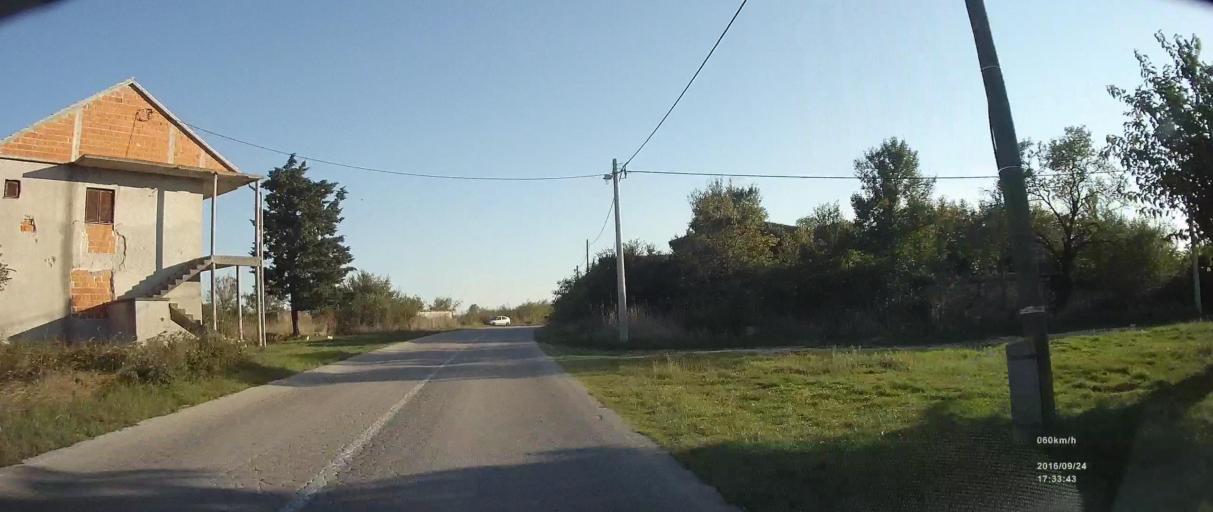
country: HR
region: Zadarska
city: Posedarje
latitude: 44.1718
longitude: 15.4576
